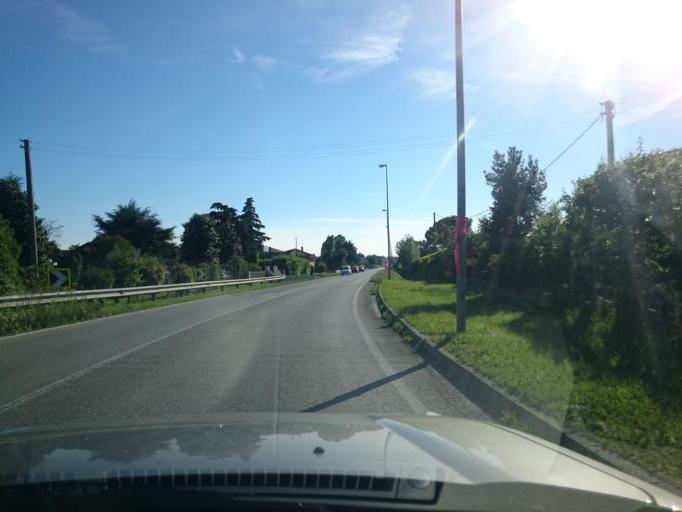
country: IT
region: Veneto
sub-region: Provincia di Venezia
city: Stigliano
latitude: 45.5216
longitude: 12.0439
